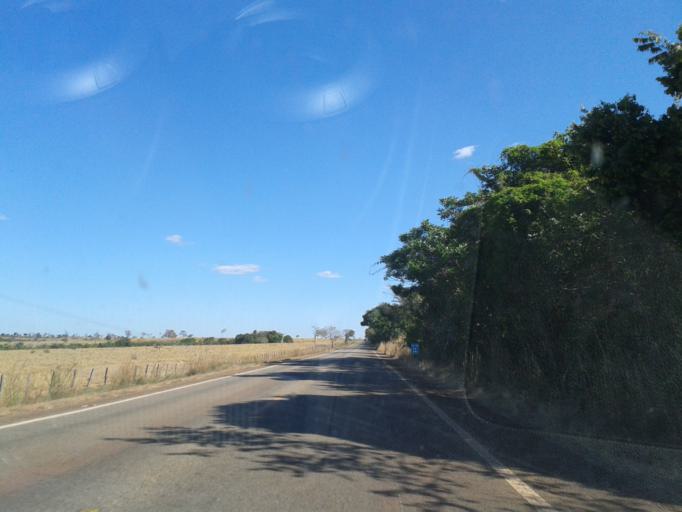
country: BR
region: Goias
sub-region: Mozarlandia
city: Mozarlandia
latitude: -14.3753
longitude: -50.4324
